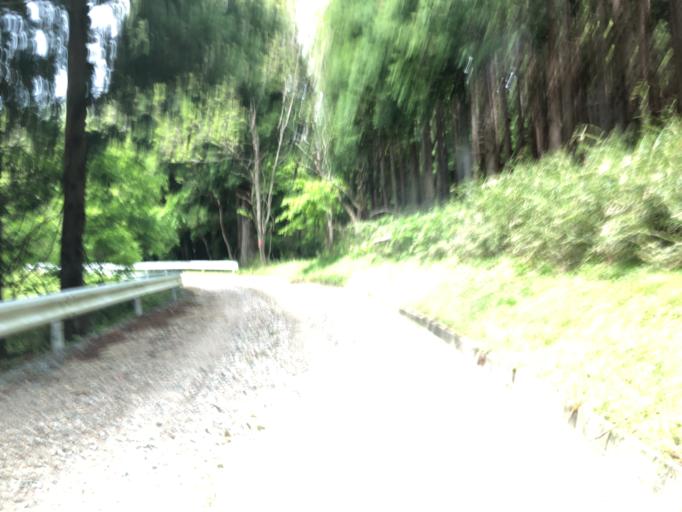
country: JP
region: Miyagi
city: Marumori
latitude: 37.7351
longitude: 140.8298
